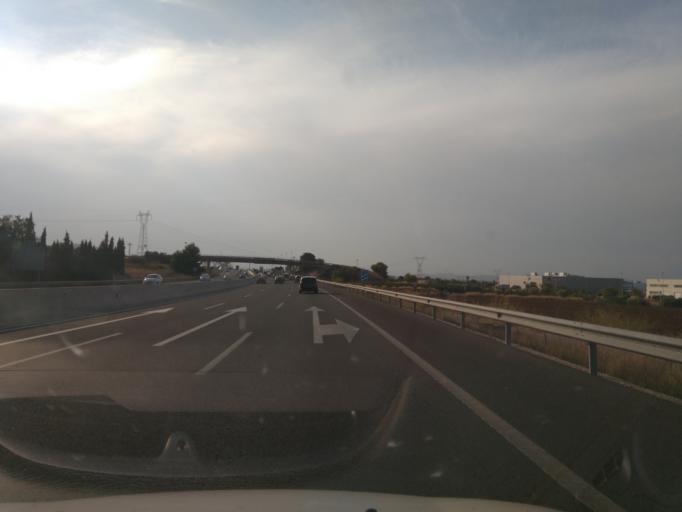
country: ES
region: Valencia
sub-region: Provincia de Valencia
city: Torrent
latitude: 39.4139
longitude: -0.5035
